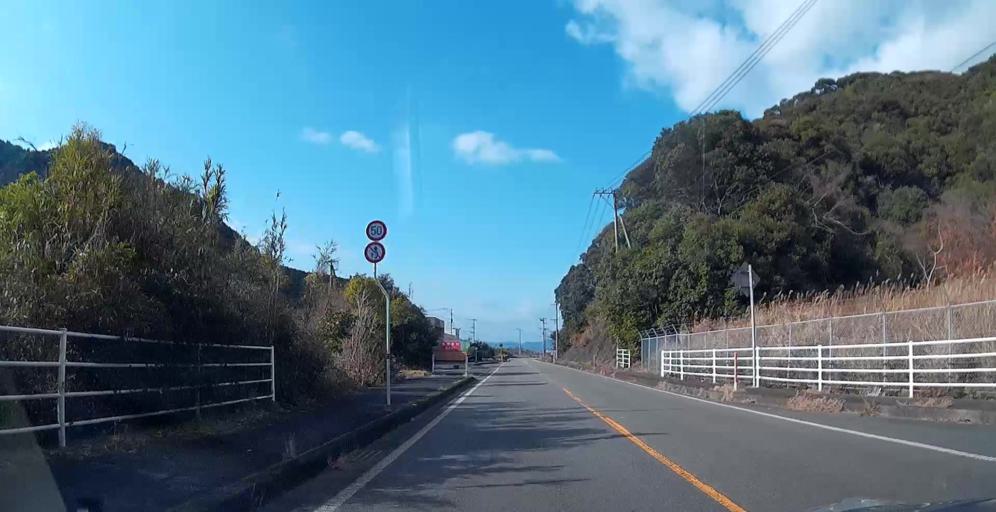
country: JP
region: Kumamoto
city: Yatsushiro
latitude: 32.4128
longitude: 130.5530
